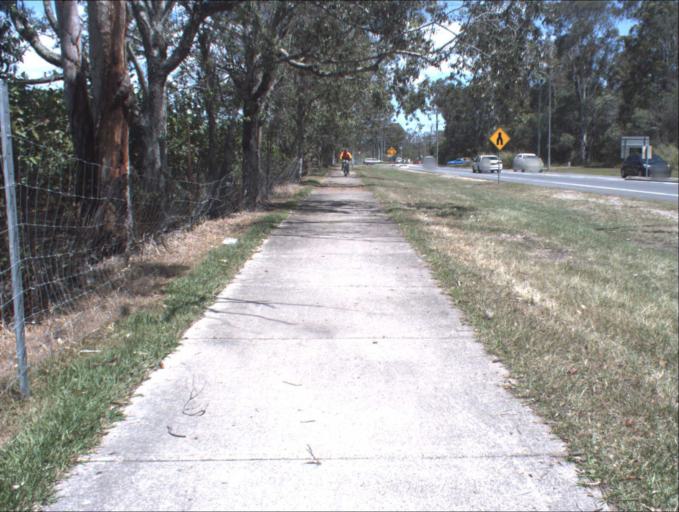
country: AU
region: Queensland
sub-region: Logan
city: Logan City
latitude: -27.6615
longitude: 153.0920
